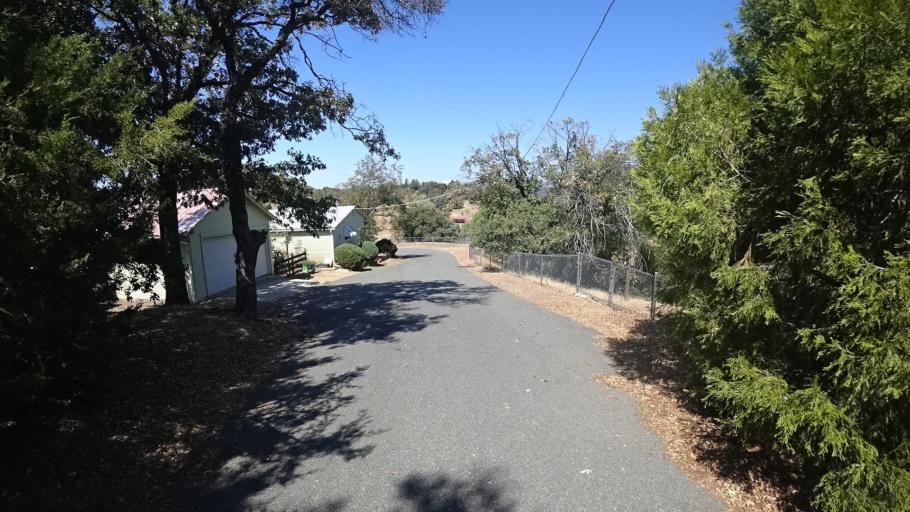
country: US
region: California
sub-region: San Diego County
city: Julian
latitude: 33.0786
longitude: -116.5892
